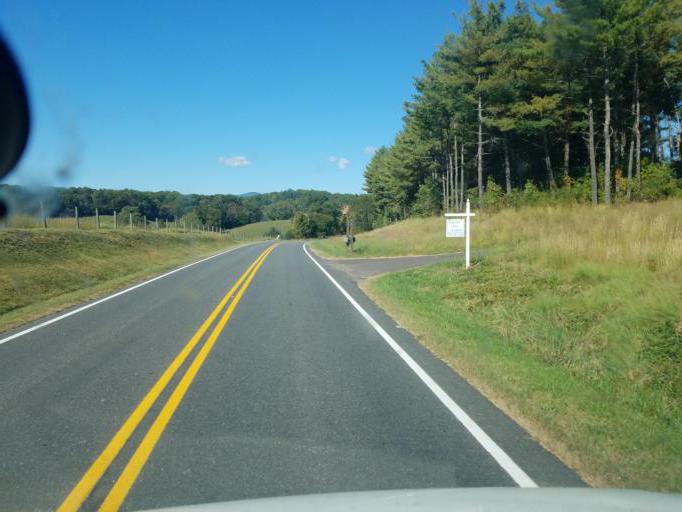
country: US
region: Virginia
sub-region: Madison County
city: Madison
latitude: 38.3488
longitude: -78.3332
